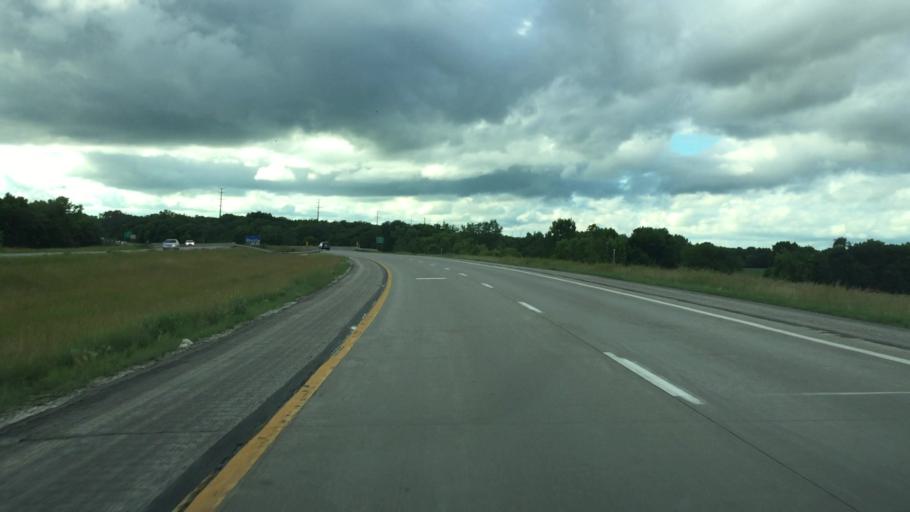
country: US
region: Iowa
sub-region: Polk County
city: Altoona
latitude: 41.6214
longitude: -93.4931
